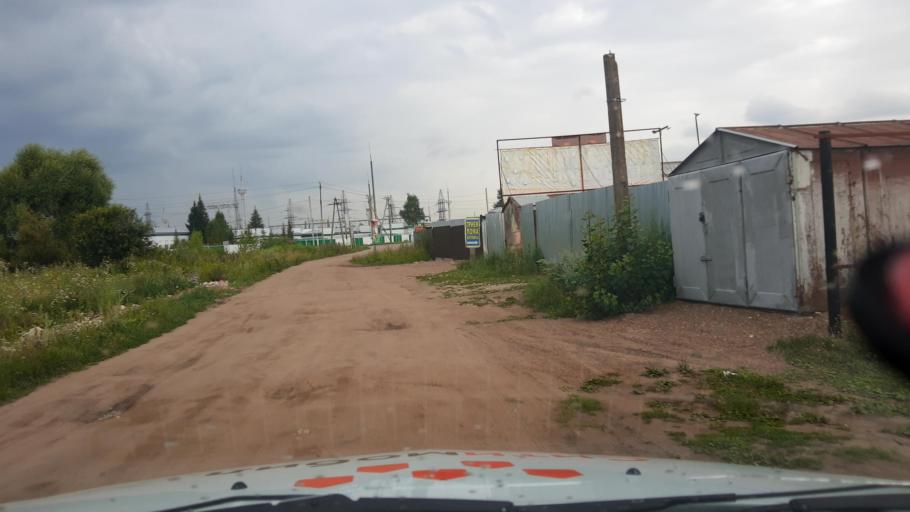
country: RU
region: Bashkortostan
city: Ufa
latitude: 54.6724
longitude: 56.0877
